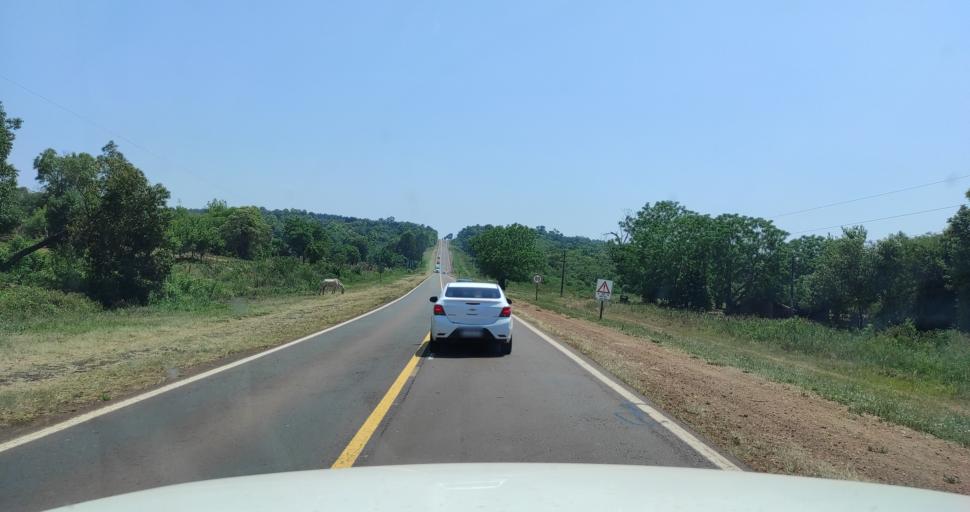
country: AR
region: Misiones
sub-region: Departamento de San Ignacio
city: San Ignacio
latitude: -27.2530
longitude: -55.5237
